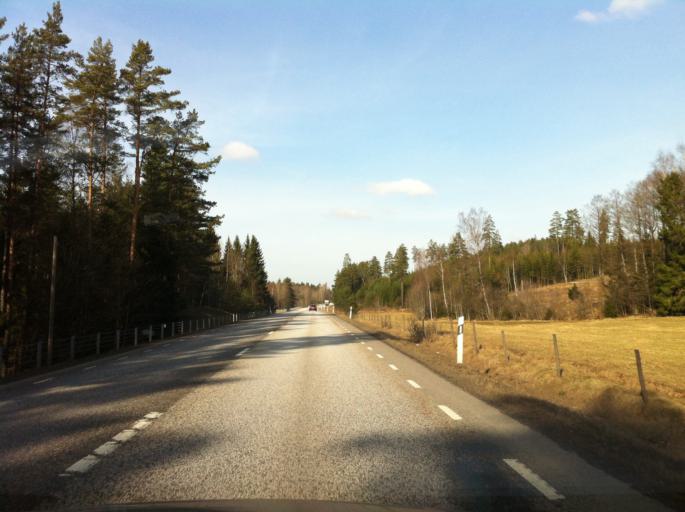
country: SE
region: Joenkoeping
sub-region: Mullsjo Kommun
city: Mullsjoe
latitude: 57.9488
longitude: 13.8360
